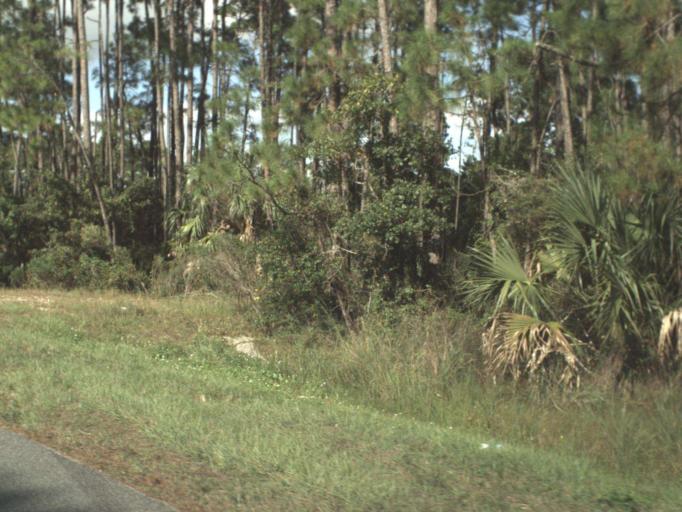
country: US
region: Florida
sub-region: Gulf County
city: Port Saint Joe
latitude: 29.7882
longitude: -85.3014
